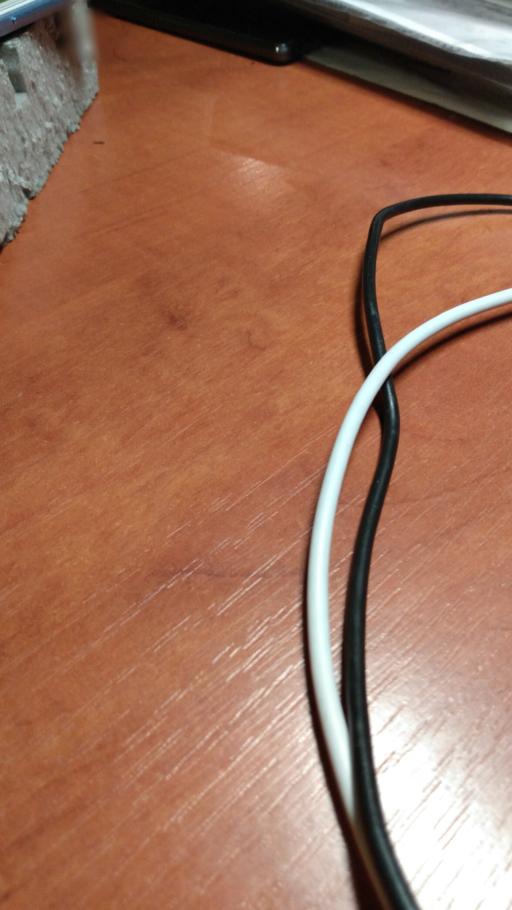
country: RU
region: Republic of Karelia
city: Pudozh
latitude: 61.9892
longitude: 37.6034
